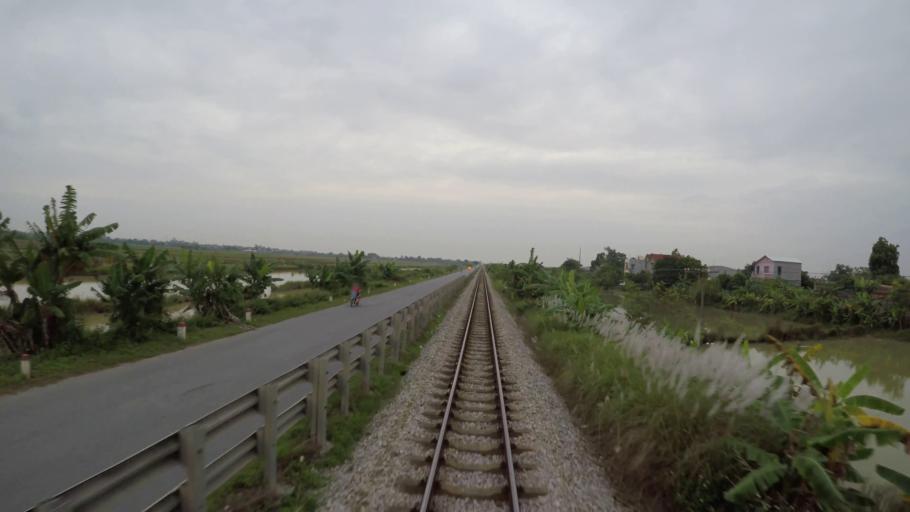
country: VN
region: Hung Yen
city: Ban Yen Nhan
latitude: 20.9792
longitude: 106.0829
